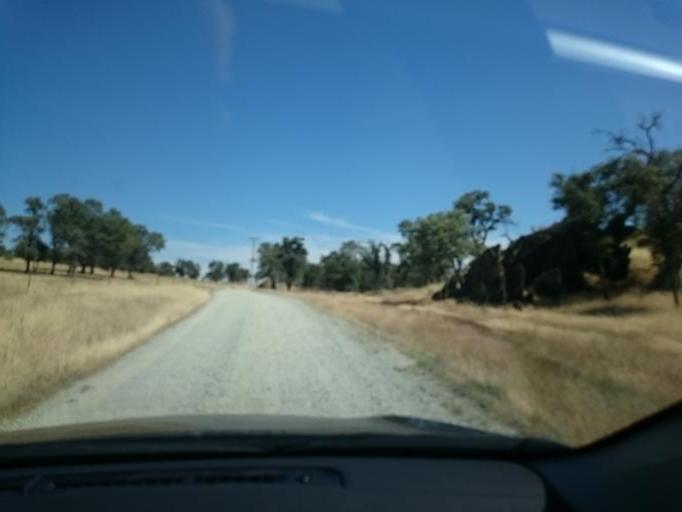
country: US
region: California
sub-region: Calaveras County
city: Rancho Calaveras
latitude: 38.0760
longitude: -120.7410
